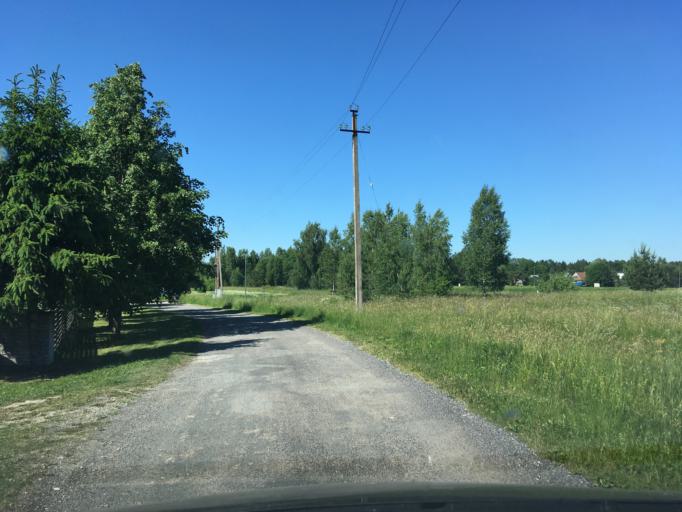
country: EE
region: Harju
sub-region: Raasiku vald
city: Raasiku
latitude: 59.1790
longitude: 25.1729
